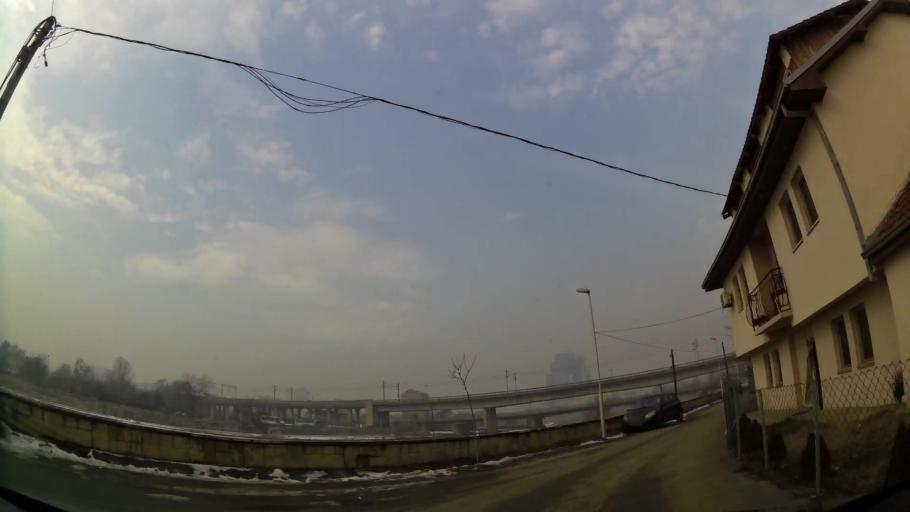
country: MK
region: Karpos
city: Skopje
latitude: 41.9941
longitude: 21.4514
